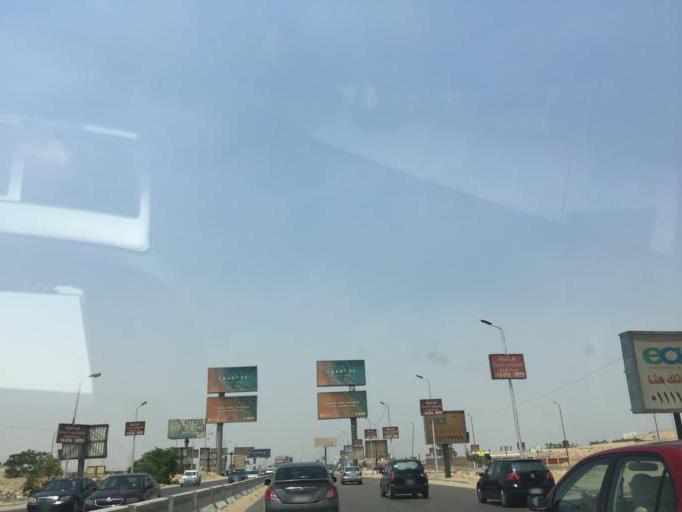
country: EG
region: Muhafazat al Qalyubiyah
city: Al Khankah
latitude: 30.0794
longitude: 31.4332
